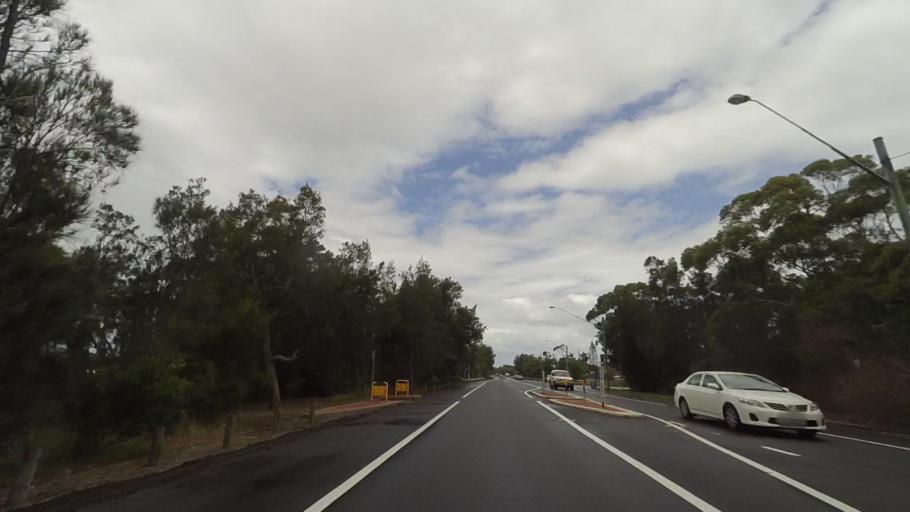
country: AU
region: New South Wales
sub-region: Wyong Shire
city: The Entrance
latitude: -33.3271
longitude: 151.5059
